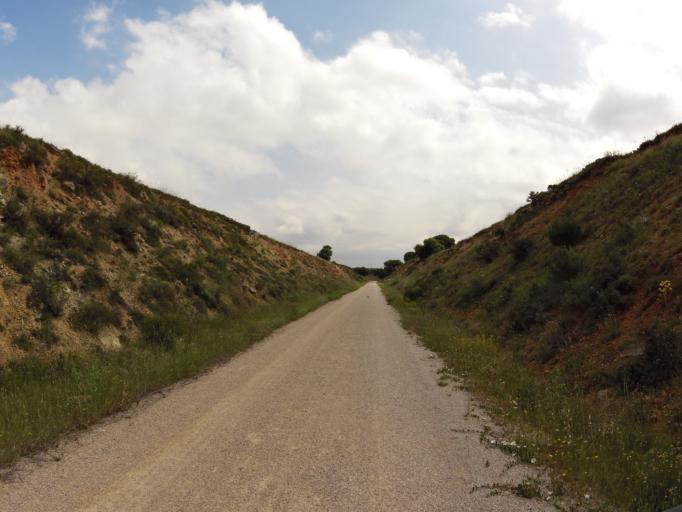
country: ES
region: Castille-La Mancha
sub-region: Provincia de Albacete
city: Robledo
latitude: 38.7730
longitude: -2.4425
